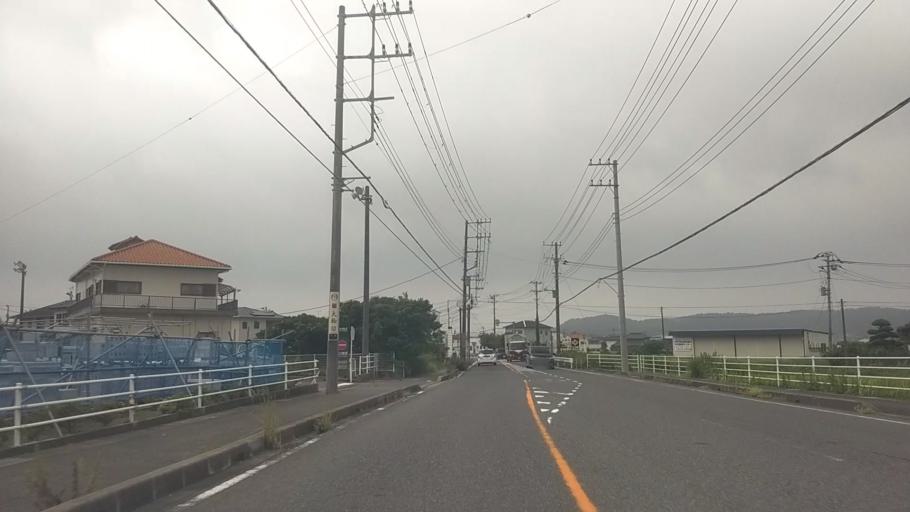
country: JP
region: Chiba
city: Kawaguchi
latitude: 35.1147
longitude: 140.0936
